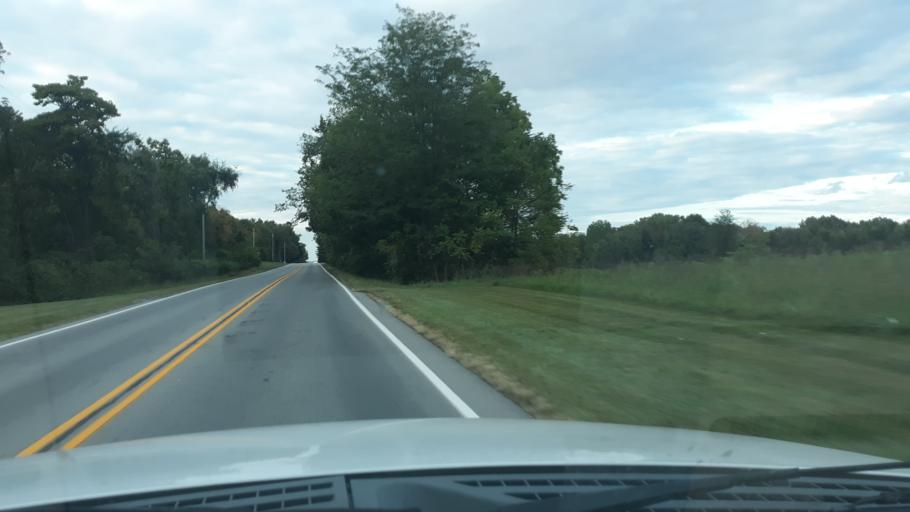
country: US
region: Illinois
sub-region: Saline County
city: Eldorado
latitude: 37.8237
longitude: -88.4524
